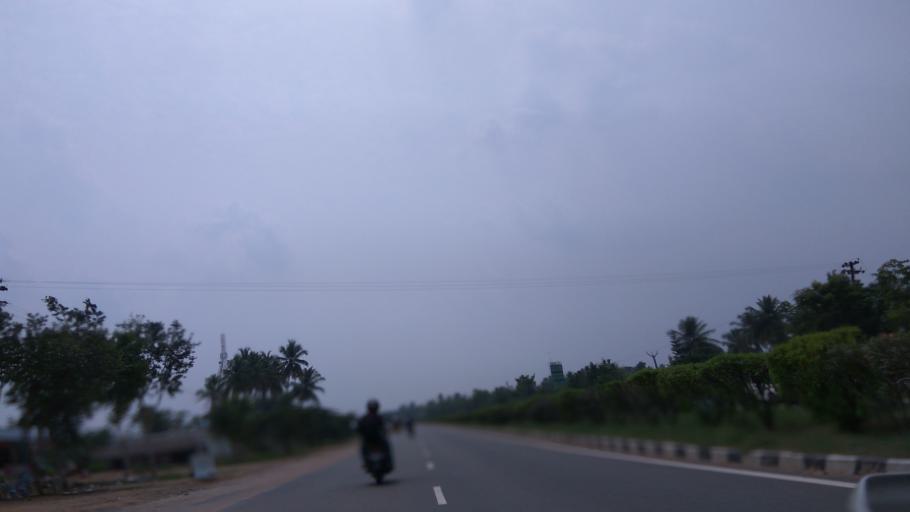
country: IN
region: Tamil Nadu
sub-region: Dharmapuri
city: Palakkodu
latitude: 12.2743
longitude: 78.1966
